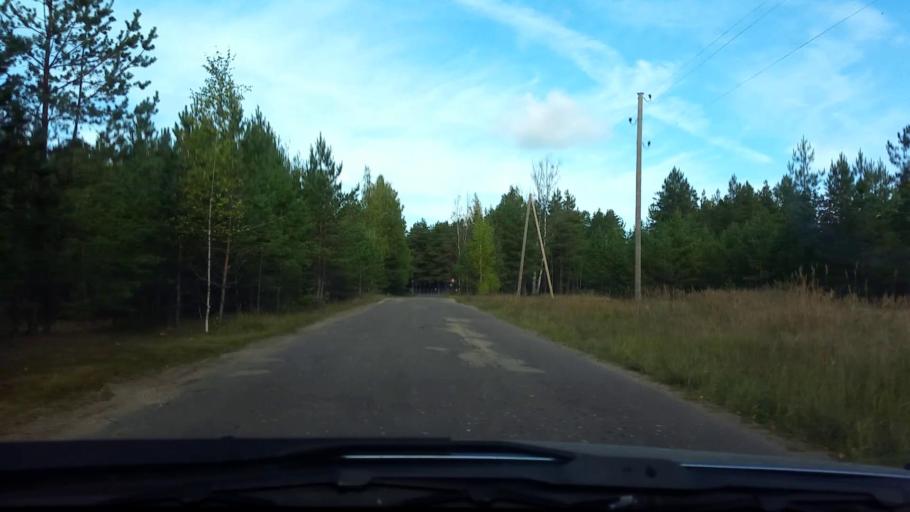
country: LV
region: Adazi
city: Adazi
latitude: 57.1211
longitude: 24.3607
